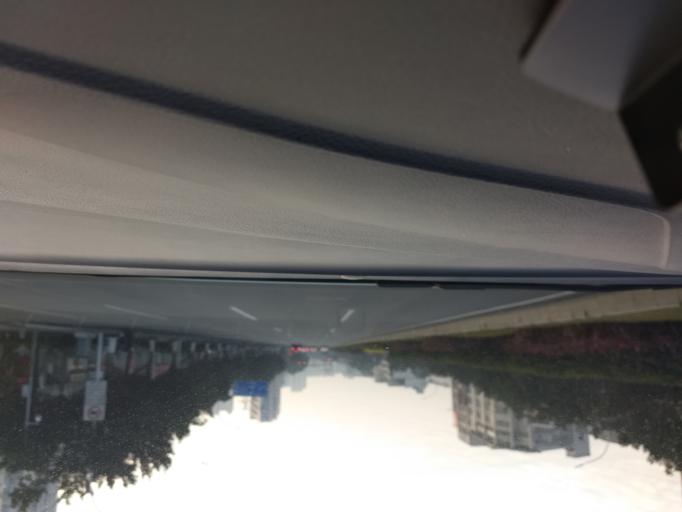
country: CN
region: Guangdong
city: Nansha
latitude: 22.8032
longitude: 113.5388
